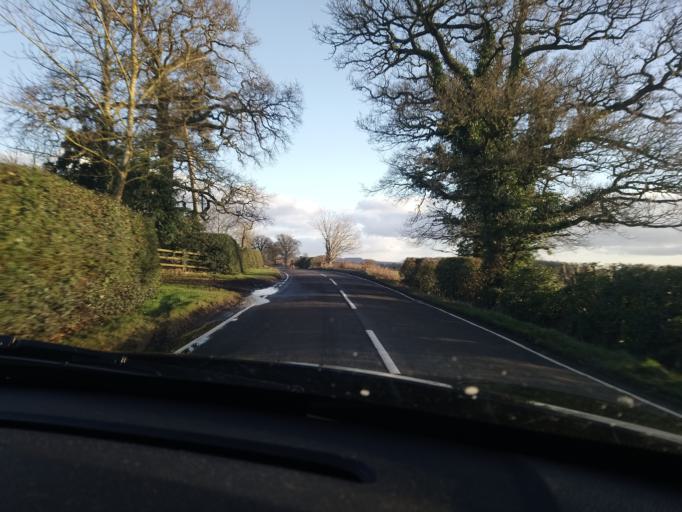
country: GB
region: England
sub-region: Shropshire
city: Wem
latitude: 52.8727
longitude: -2.7787
